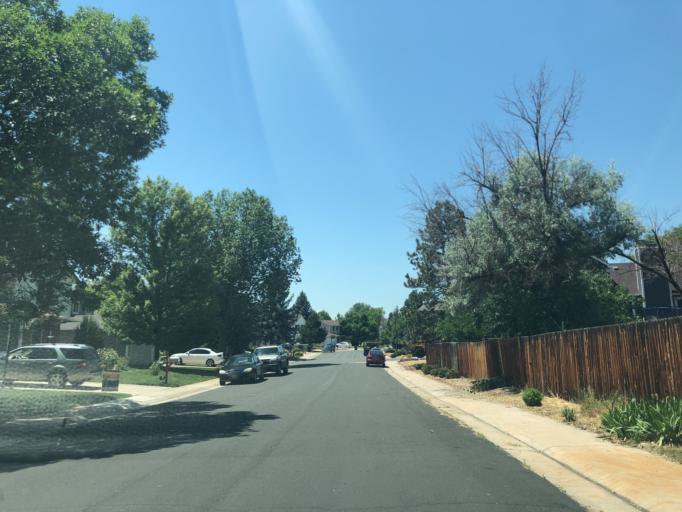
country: US
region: Colorado
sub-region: Arapahoe County
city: Dove Valley
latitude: 39.6208
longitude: -104.7764
